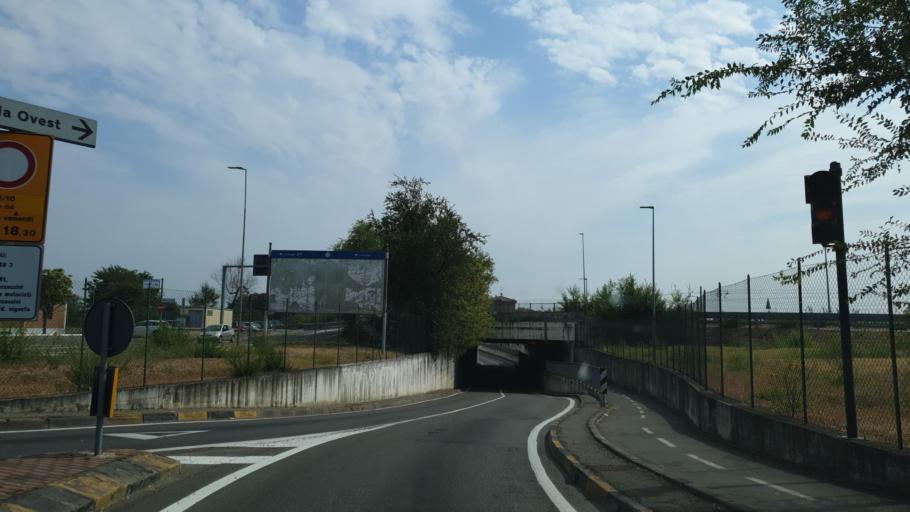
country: IT
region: Emilia-Romagna
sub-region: Provincia di Parma
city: Vicofertile
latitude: 44.8162
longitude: 10.2885
